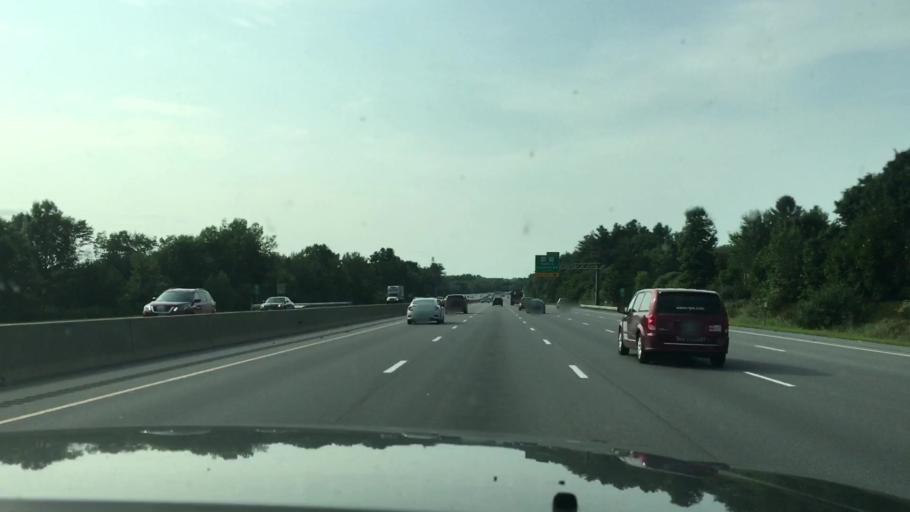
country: US
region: New Hampshire
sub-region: Hillsborough County
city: Nashua
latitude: 42.7365
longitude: -71.4791
